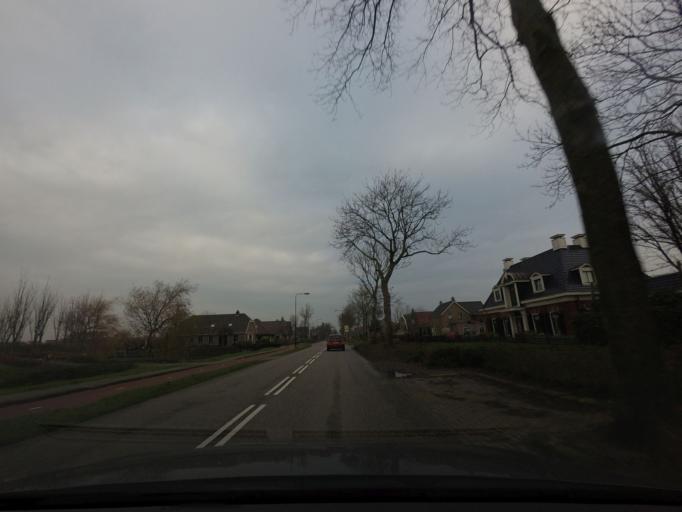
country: NL
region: North Holland
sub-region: Gemeente Heerhugowaard
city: Heerhugowaard
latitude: 52.7017
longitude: 4.8514
